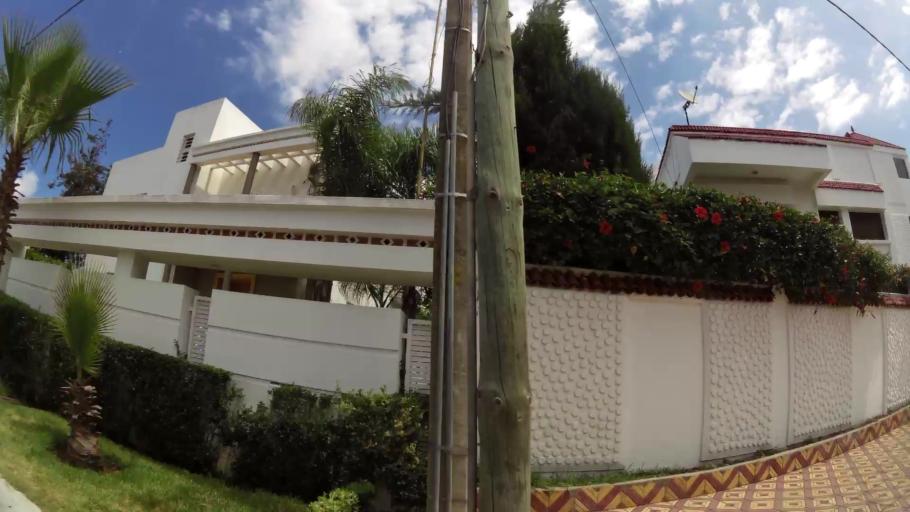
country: MA
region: Gharb-Chrarda-Beni Hssen
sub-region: Kenitra Province
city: Kenitra
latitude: 34.2666
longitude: -6.5965
